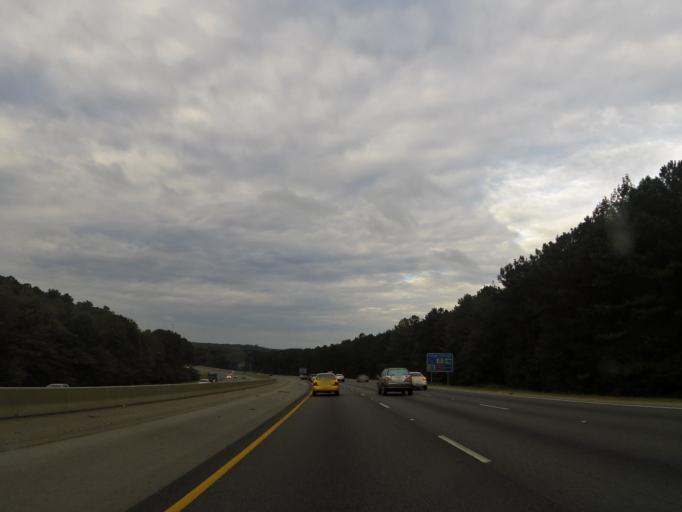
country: US
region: Alabama
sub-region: Shelby County
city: Indian Springs Village
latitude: 33.3269
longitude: -86.7815
